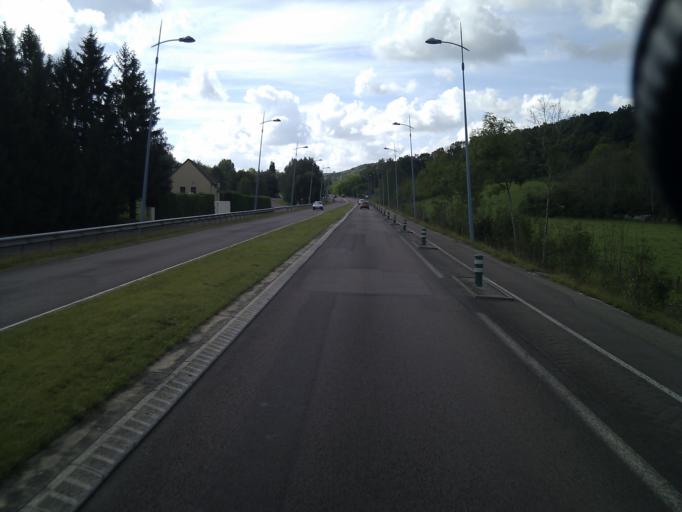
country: FR
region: Bourgogne
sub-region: Departement de la Cote-d'Or
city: Montbard
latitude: 47.6298
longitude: 4.3314
